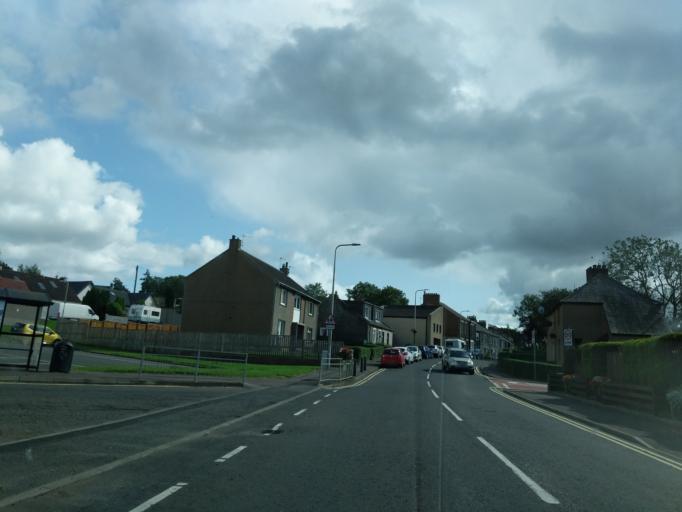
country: GB
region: Scotland
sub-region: Fife
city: Townhill
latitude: 56.0906
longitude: -3.4394
